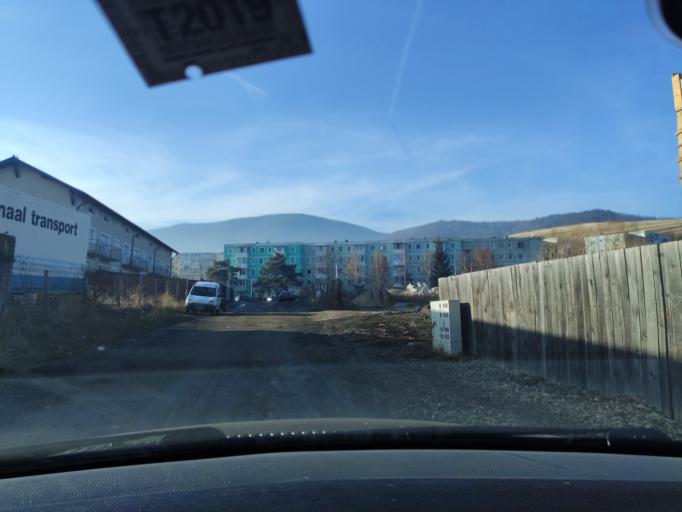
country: RO
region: Brasov
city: Codlea
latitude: 45.7068
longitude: 25.4540
